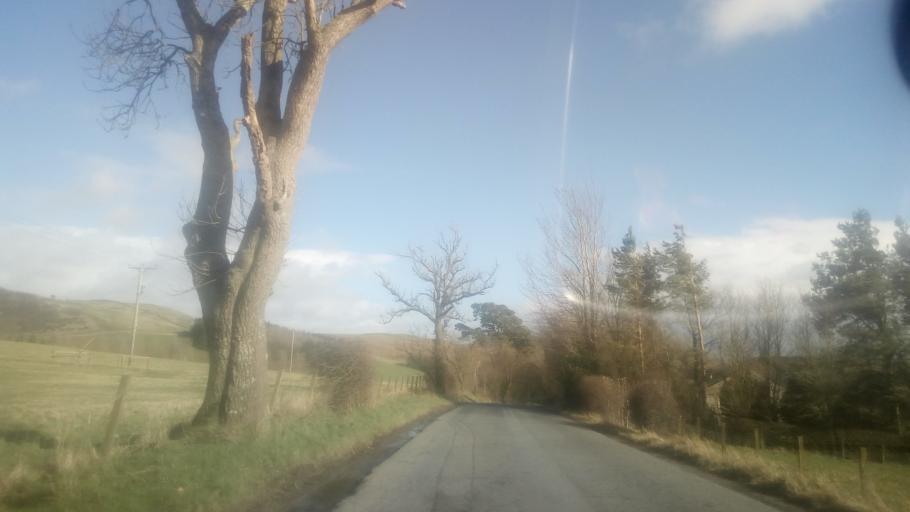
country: GB
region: Scotland
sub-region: The Scottish Borders
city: Hawick
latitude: 55.4186
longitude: -2.8741
